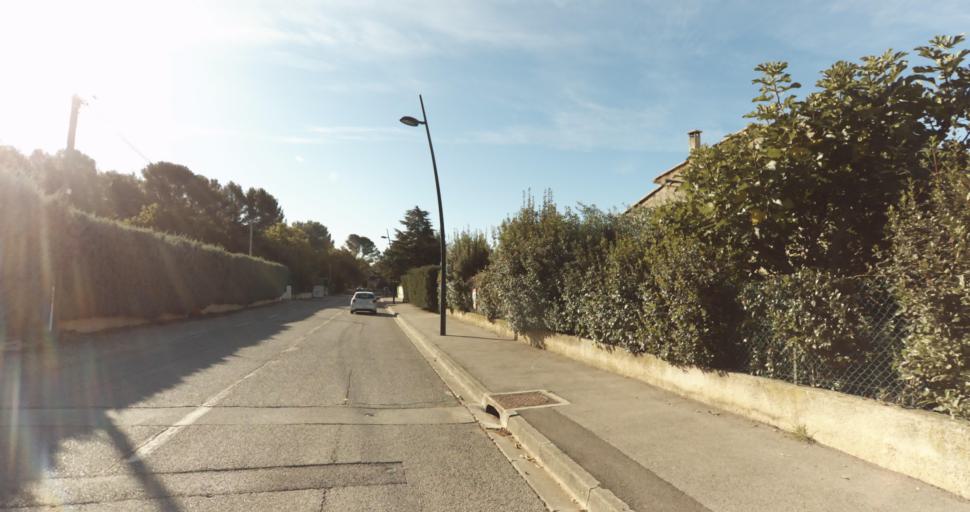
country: FR
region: Provence-Alpes-Cote d'Azur
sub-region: Departement des Bouches-du-Rhone
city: Venelles
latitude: 43.5909
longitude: 5.4721
